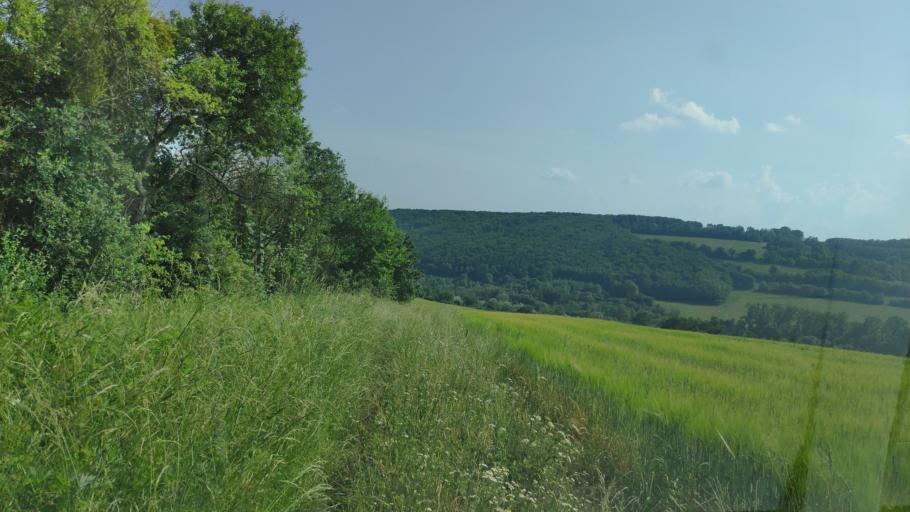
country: SK
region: Presovsky
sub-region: Okres Presov
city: Presov
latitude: 48.9611
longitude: 21.1546
